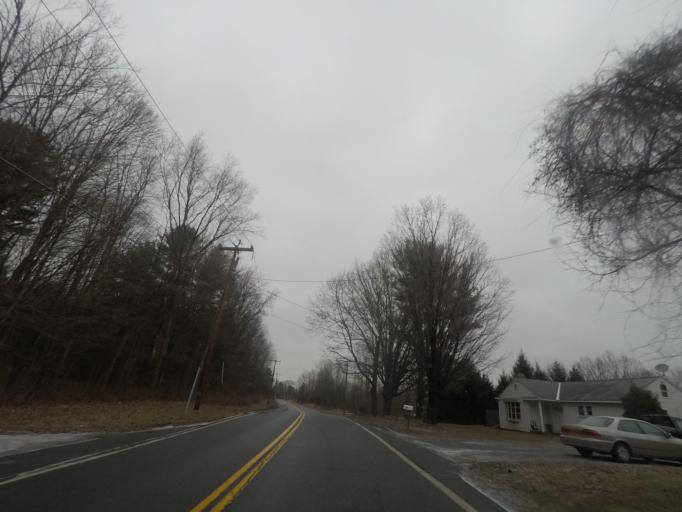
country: US
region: New York
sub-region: Saratoga County
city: Country Knolls
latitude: 42.9123
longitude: -73.7720
